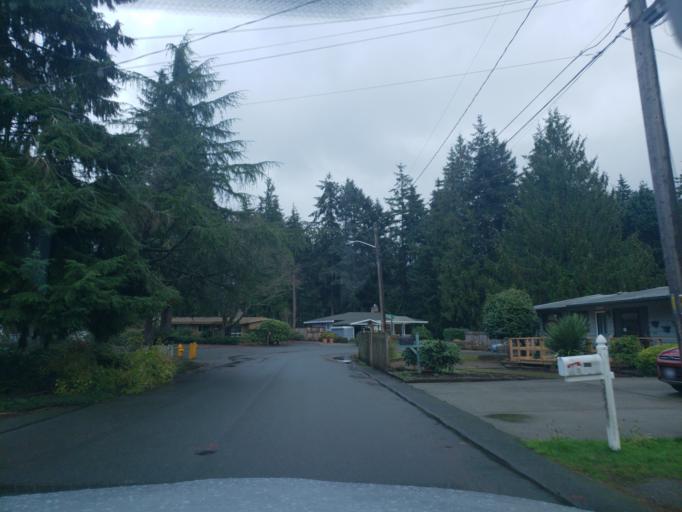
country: US
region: Washington
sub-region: Snohomish County
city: Esperance
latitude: 47.7728
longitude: -122.3586
